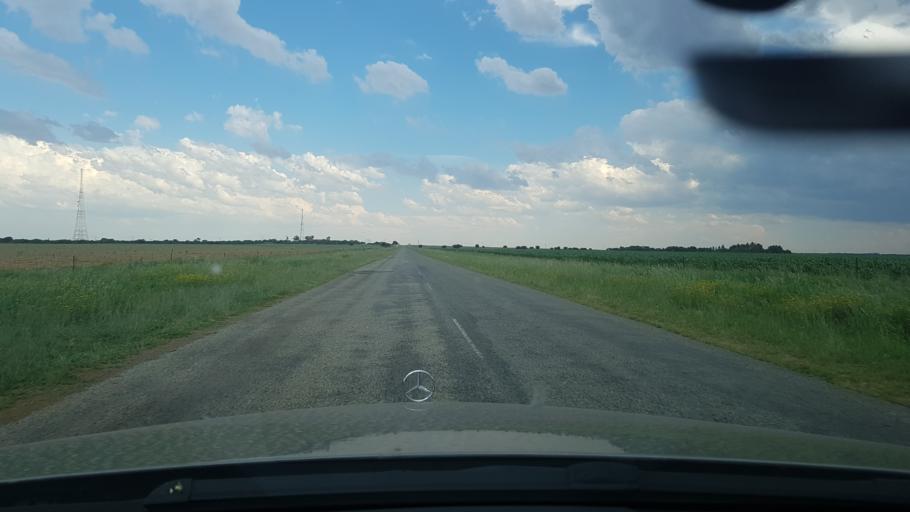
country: ZA
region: Orange Free State
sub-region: Lejweleputswa District Municipality
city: Hoopstad
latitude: -27.9450
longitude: 25.6983
